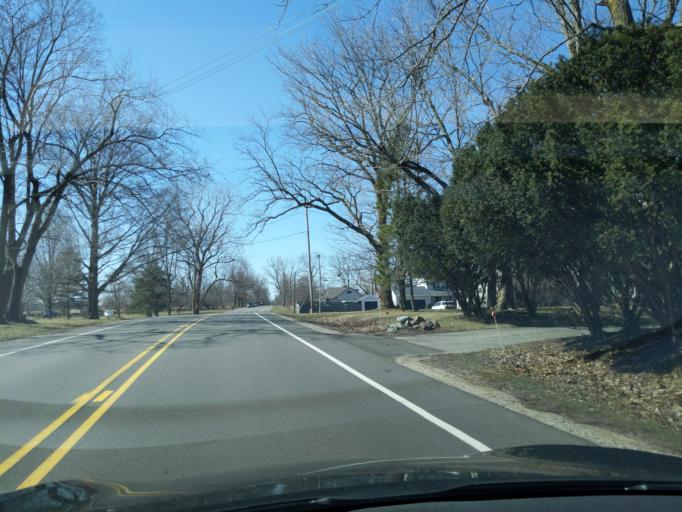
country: US
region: Michigan
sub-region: Eaton County
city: Grand Ledge
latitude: 42.7264
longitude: -84.7040
